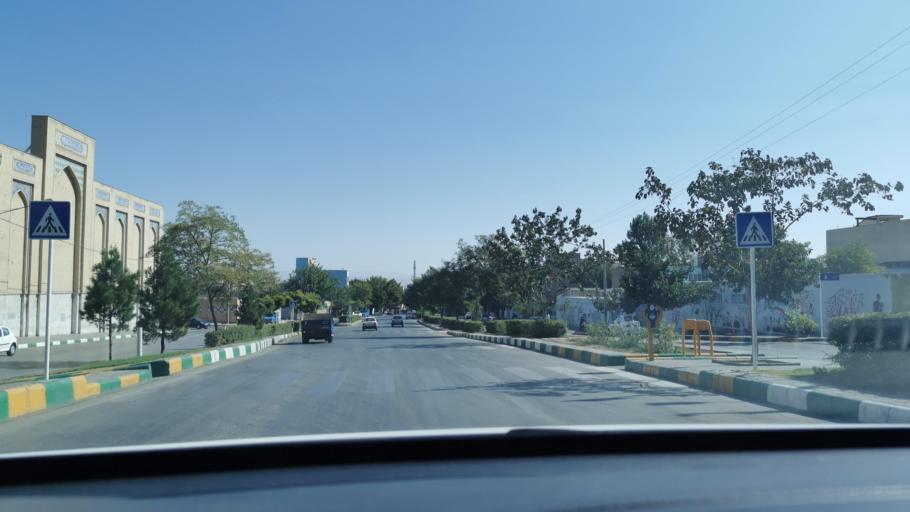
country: IR
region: Razavi Khorasan
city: Mashhad
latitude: 36.3426
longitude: 59.6319
